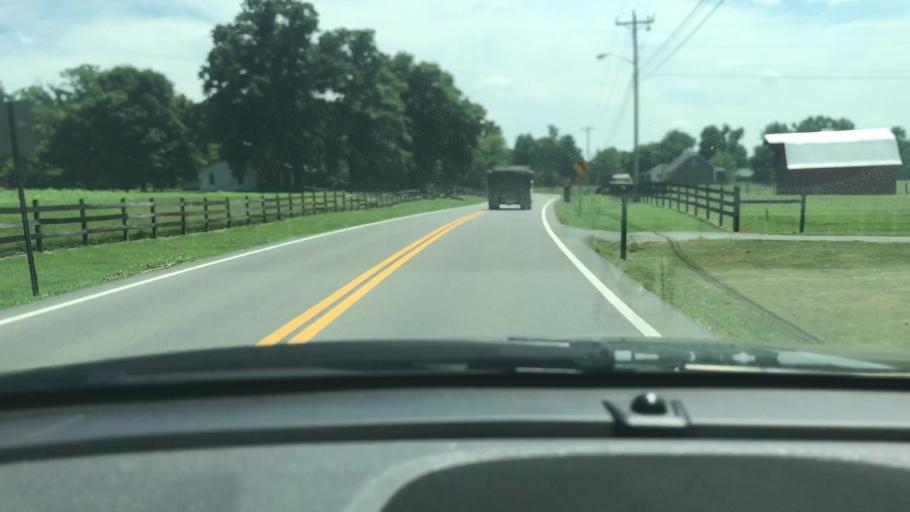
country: US
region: Tennessee
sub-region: Sumner County
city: White House
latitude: 36.4538
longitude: -86.6467
